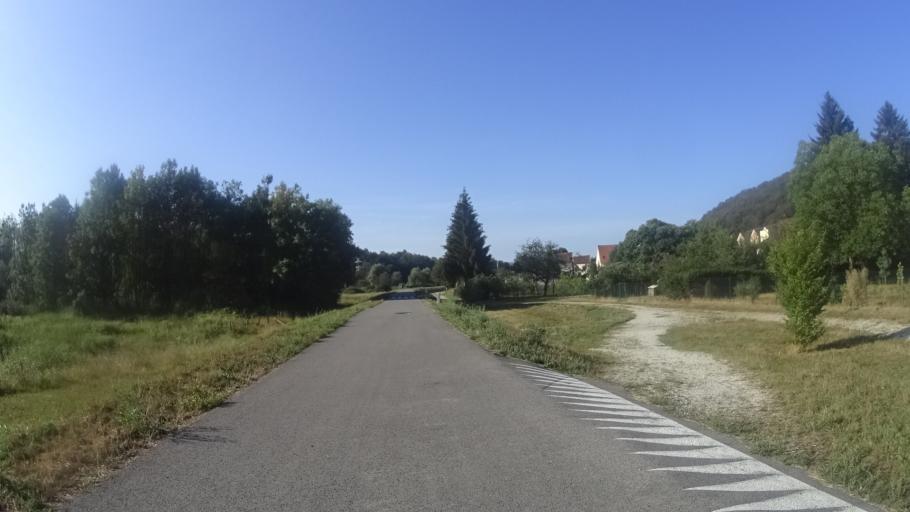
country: FR
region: Franche-Comte
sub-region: Departement du Doubs
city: Bart
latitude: 47.4910
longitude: 6.7733
